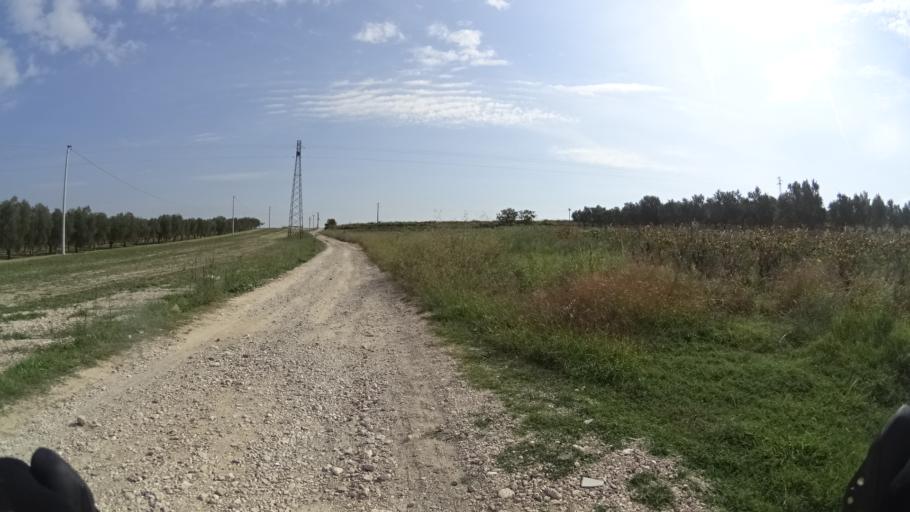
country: IT
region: Apulia
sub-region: Provincia di Taranto
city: San Marzano di San Giuseppe
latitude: 40.4652
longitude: 17.4734
